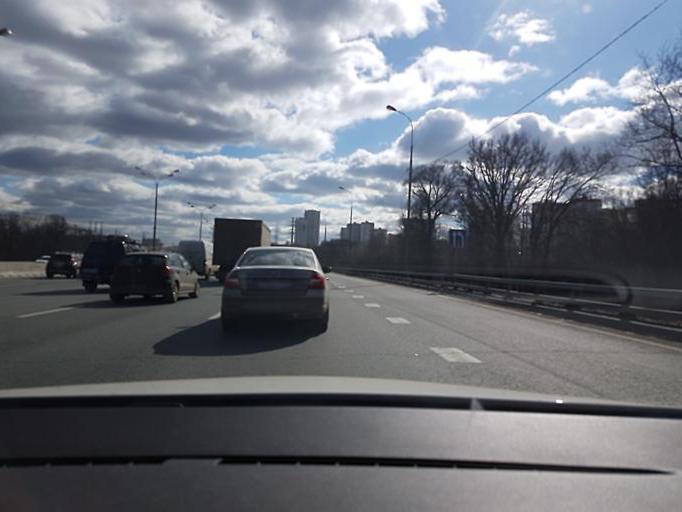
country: RU
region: Moscow
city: Strogino
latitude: 55.8468
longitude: 37.3915
